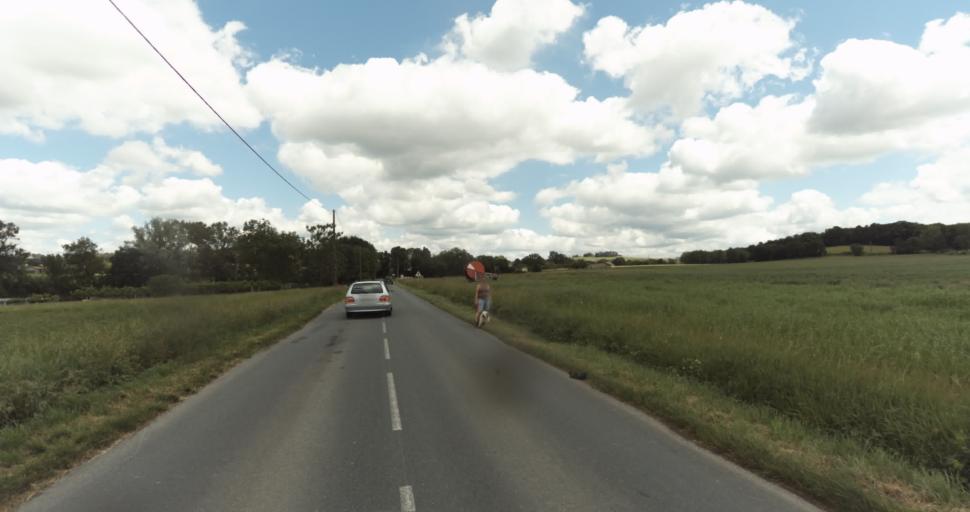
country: FR
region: Aquitaine
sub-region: Departement de la Dordogne
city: Beaumont-du-Perigord
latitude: 44.7217
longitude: 0.7560
